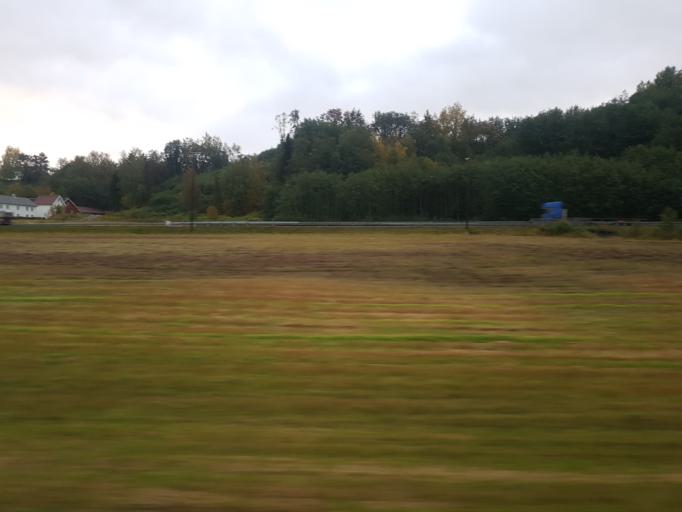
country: NO
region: Sor-Trondelag
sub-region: Melhus
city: Lundamo
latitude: 63.1364
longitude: 10.2584
